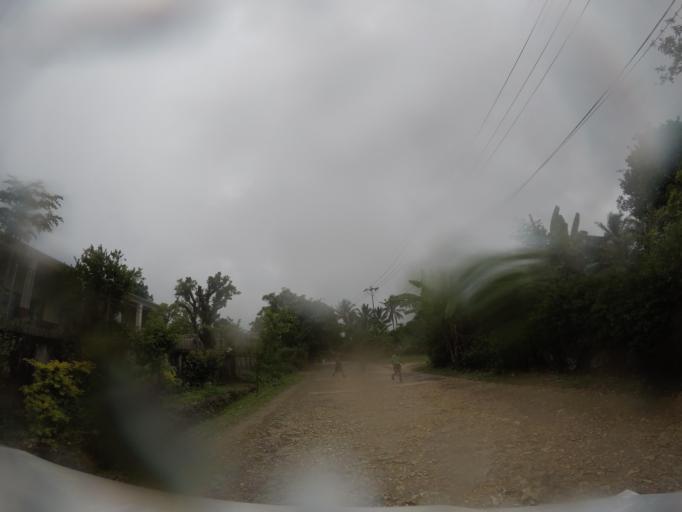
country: TL
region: Baucau
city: Venilale
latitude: -8.6410
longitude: 126.3802
